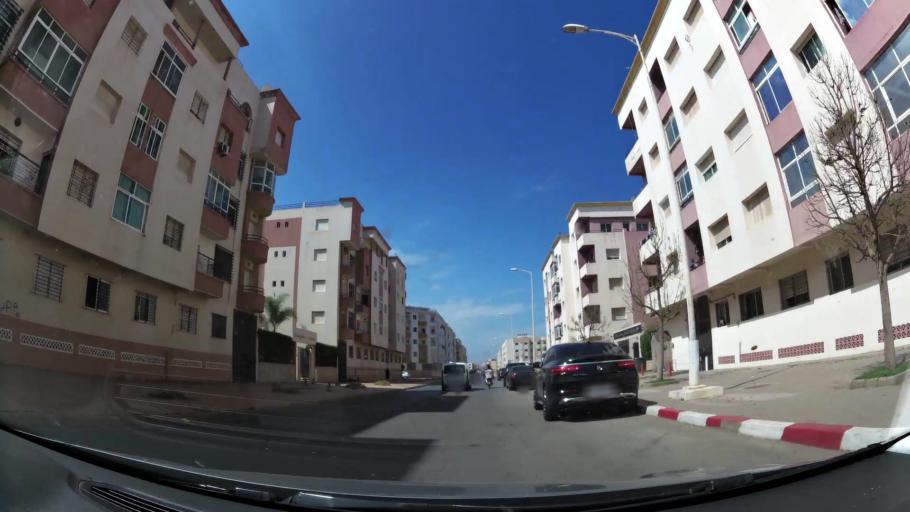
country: MA
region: Rabat-Sale-Zemmour-Zaer
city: Sale
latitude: 34.0756
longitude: -6.7924
